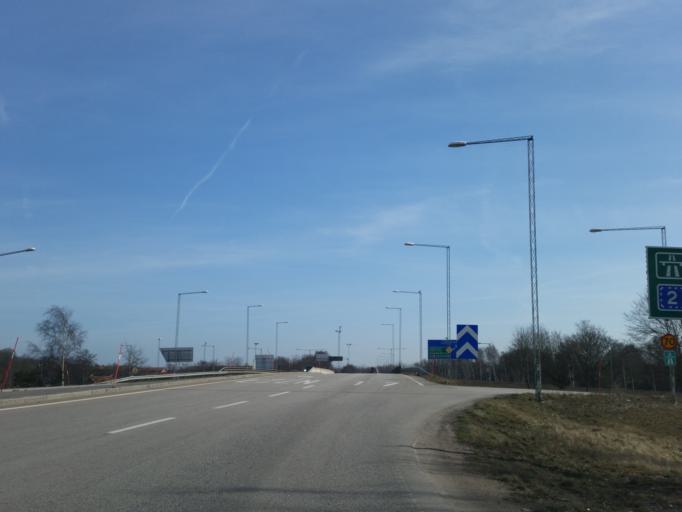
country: SE
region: Kalmar
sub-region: Kalmar Kommun
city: Kalmar
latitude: 56.6828
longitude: 16.3253
